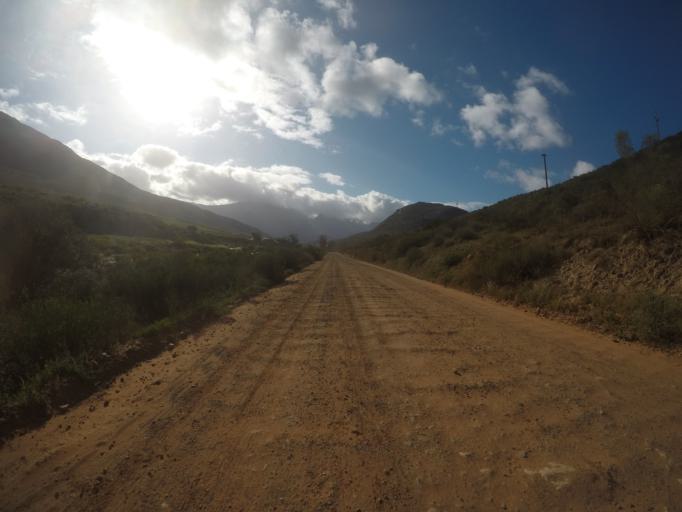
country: ZA
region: Western Cape
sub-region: West Coast District Municipality
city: Clanwilliam
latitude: -32.3645
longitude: 18.9481
